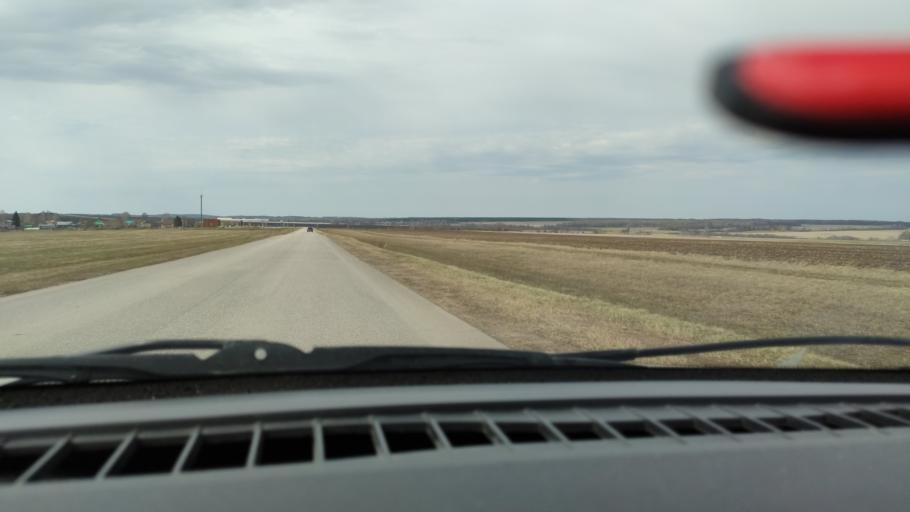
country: RU
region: Bashkortostan
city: Dyurtyuli
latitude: 55.6557
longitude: 55.0319
